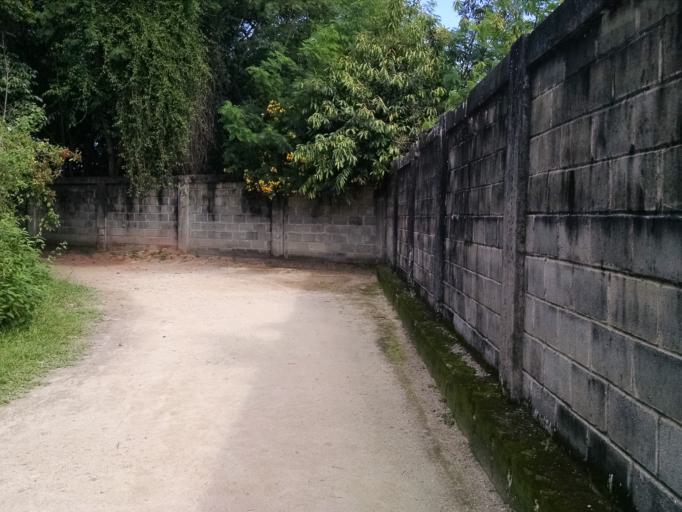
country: BR
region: Rio de Janeiro
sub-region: Sao Joao De Meriti
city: Sao Joao de Meriti
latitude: -22.9937
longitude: -43.3759
